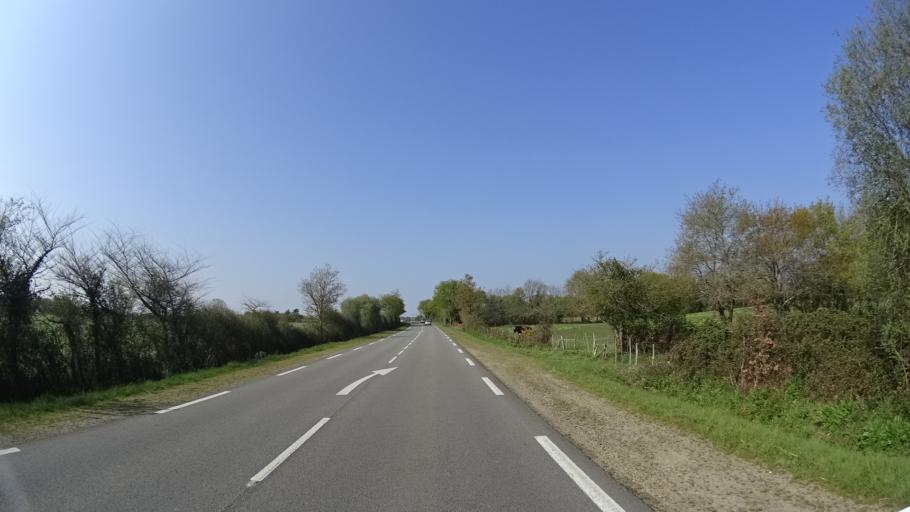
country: FR
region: Pays de la Loire
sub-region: Departement de la Loire-Atlantique
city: Saint-Hilaire-de-Chaleons
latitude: 47.0712
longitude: -1.8996
